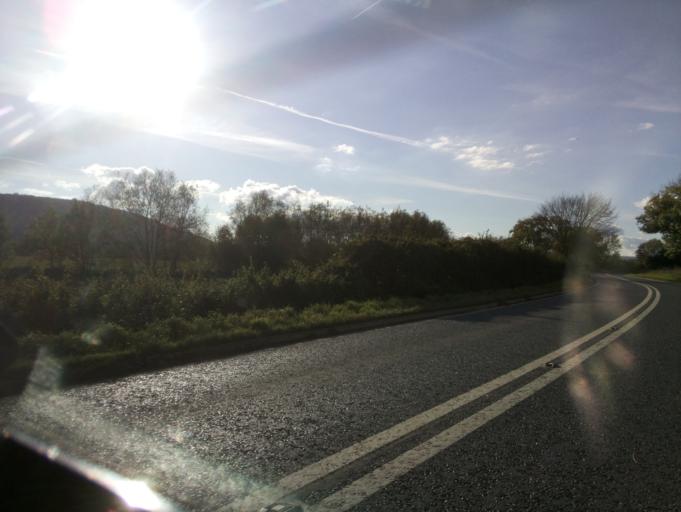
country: GB
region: England
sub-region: Herefordshire
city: Kinnersley
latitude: 52.1184
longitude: -2.9846
